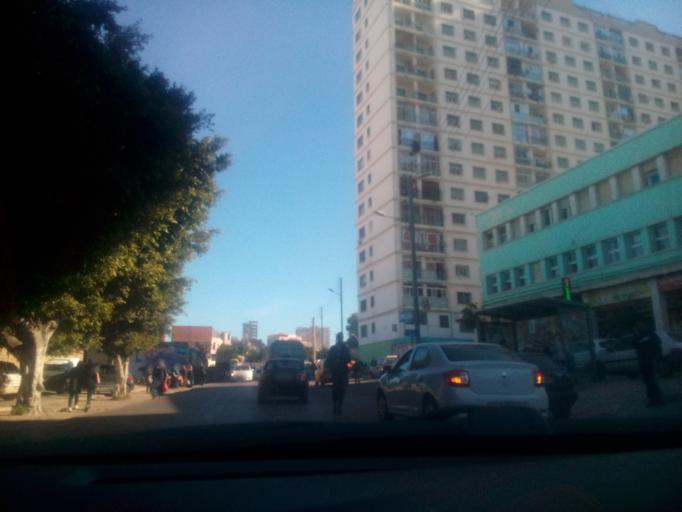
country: DZ
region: Oran
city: Oran
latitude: 35.7073
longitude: -0.6175
